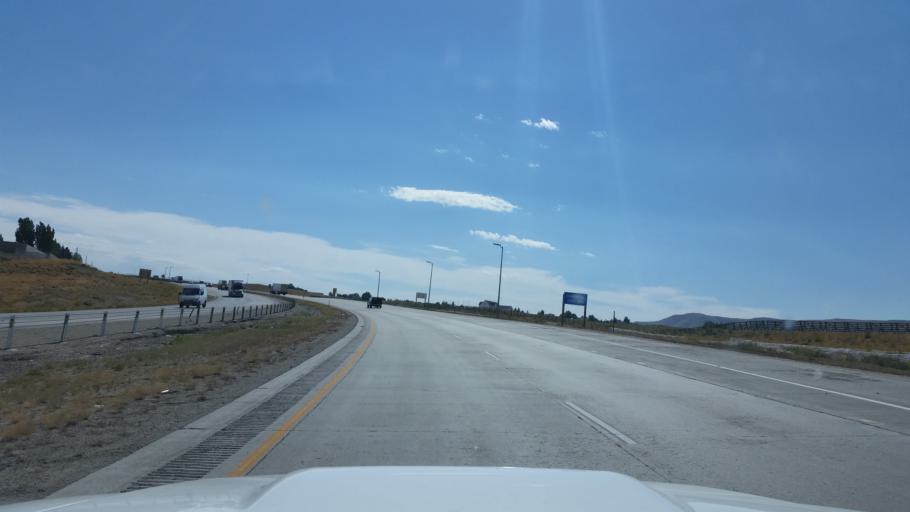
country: US
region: Wyoming
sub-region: Sweetwater County
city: Rock Springs
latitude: 41.6049
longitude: -109.2367
